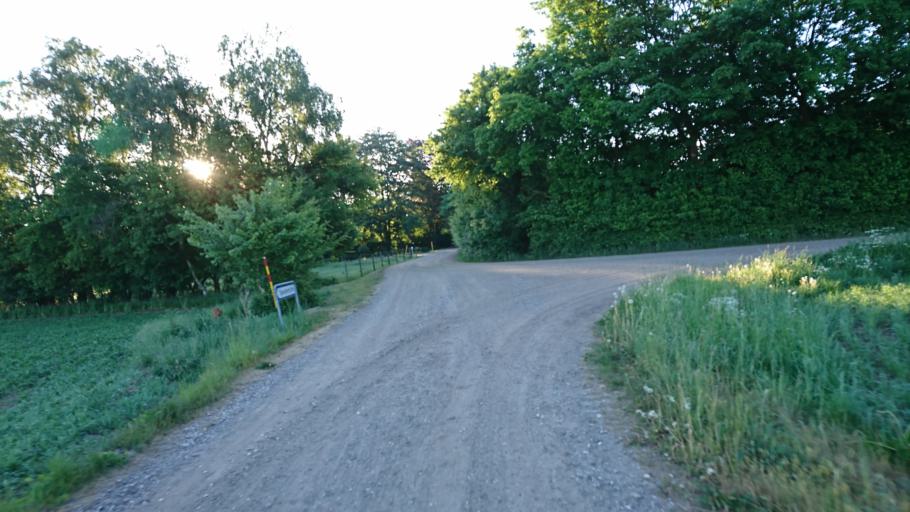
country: DK
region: Capital Region
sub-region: Egedal Kommune
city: Smorumnedre
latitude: 55.7351
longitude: 12.3213
